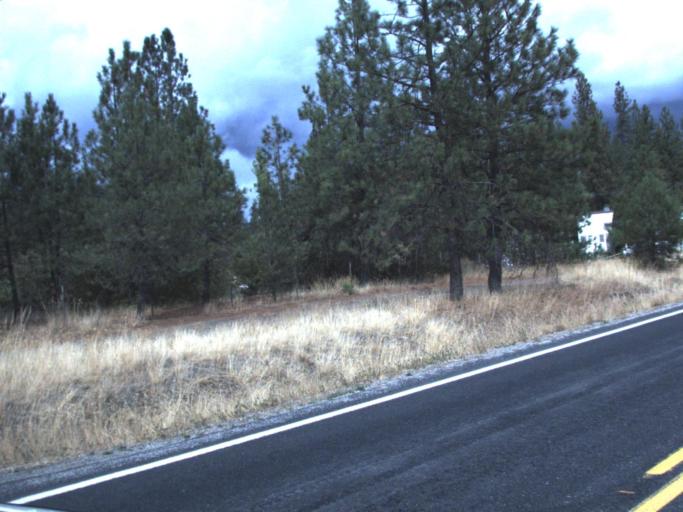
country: US
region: Washington
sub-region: Spokane County
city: Fairchild Air Force Base
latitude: 47.9034
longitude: -117.8169
